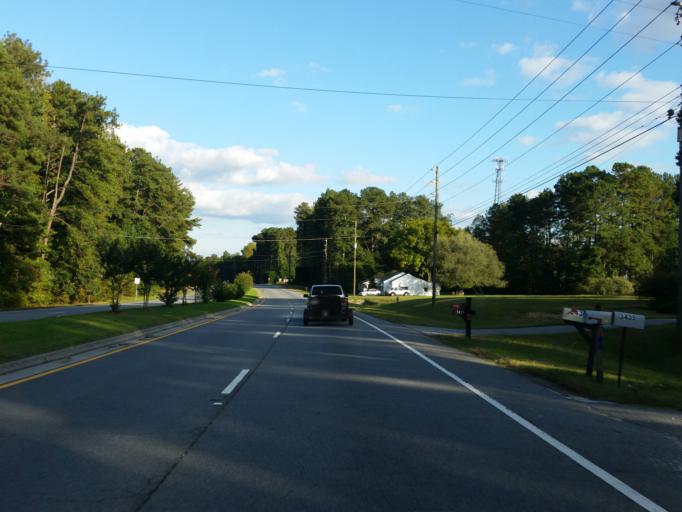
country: US
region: Georgia
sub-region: Cobb County
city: Powder Springs
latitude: 33.8976
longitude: -84.6535
